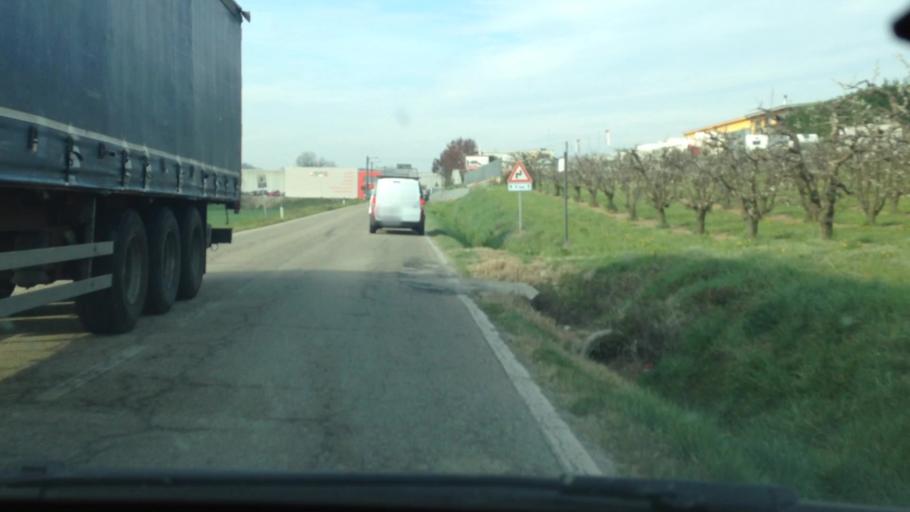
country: IT
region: Piedmont
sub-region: Provincia di Cuneo
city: Castellinaldo
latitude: 44.8076
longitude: 8.0335
